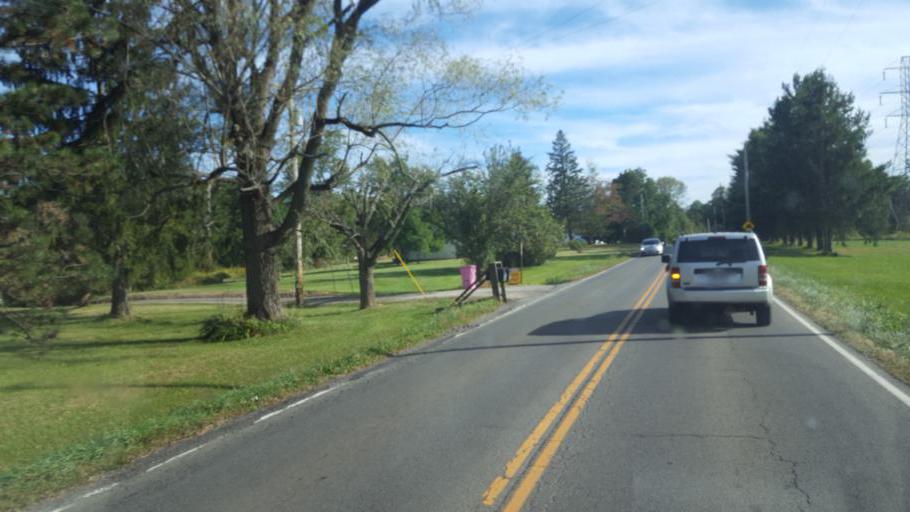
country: US
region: Ohio
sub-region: Richland County
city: Ontario
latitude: 40.7234
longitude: -82.5849
